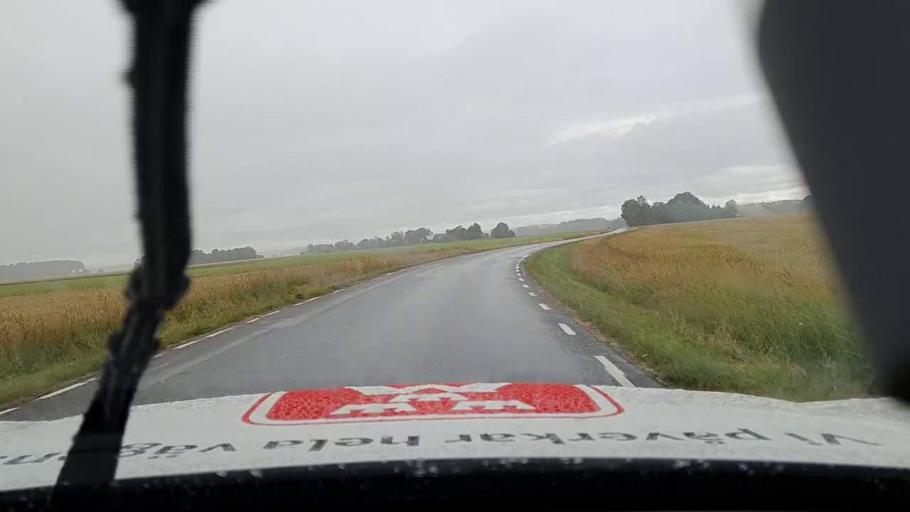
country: SE
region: Vaestra Goetaland
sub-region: Toreboda Kommun
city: Toereboda
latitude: 58.6542
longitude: 14.1083
